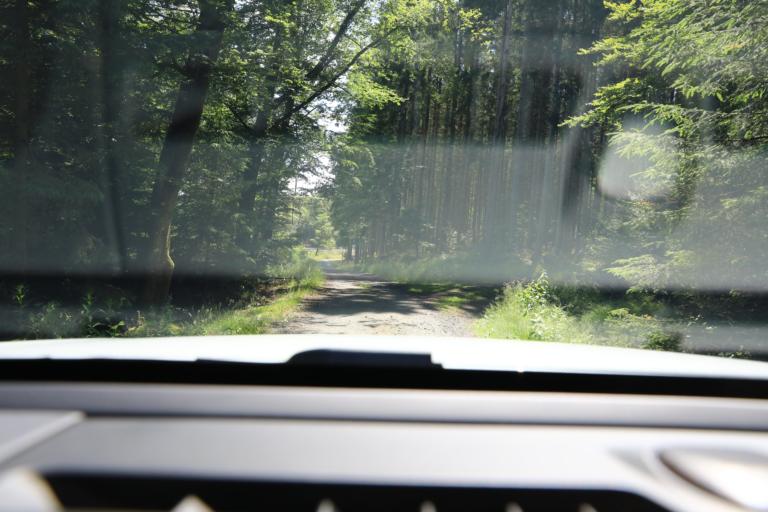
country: SE
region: Halland
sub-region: Varbergs Kommun
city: Tvaaker
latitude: 57.0934
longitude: 12.4928
